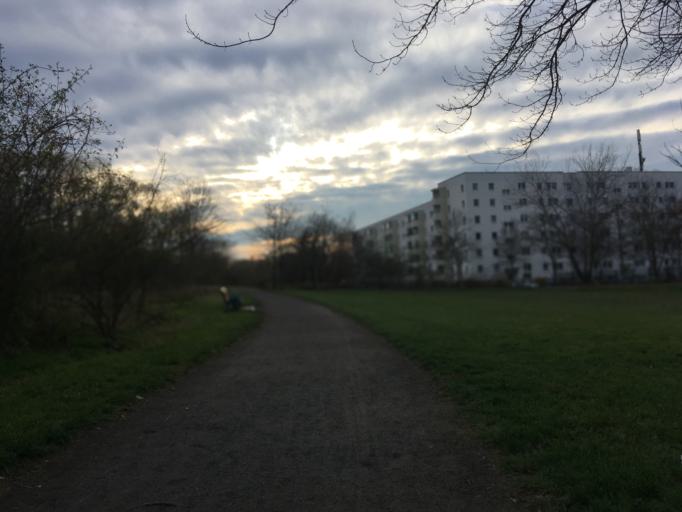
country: DE
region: Berlin
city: Falkenberg
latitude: 52.5669
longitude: 13.5343
